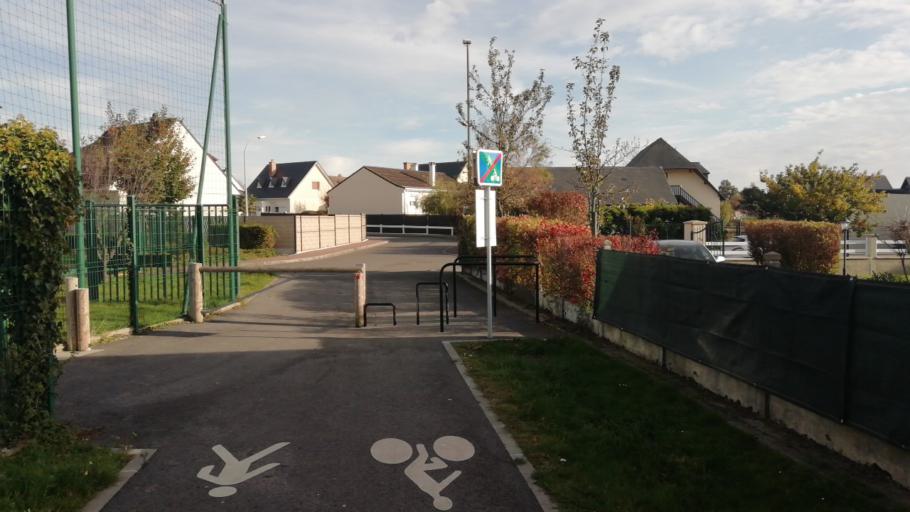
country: FR
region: Haute-Normandie
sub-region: Departement de la Seine-Maritime
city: Rogerville
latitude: 49.5064
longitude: 0.2639
